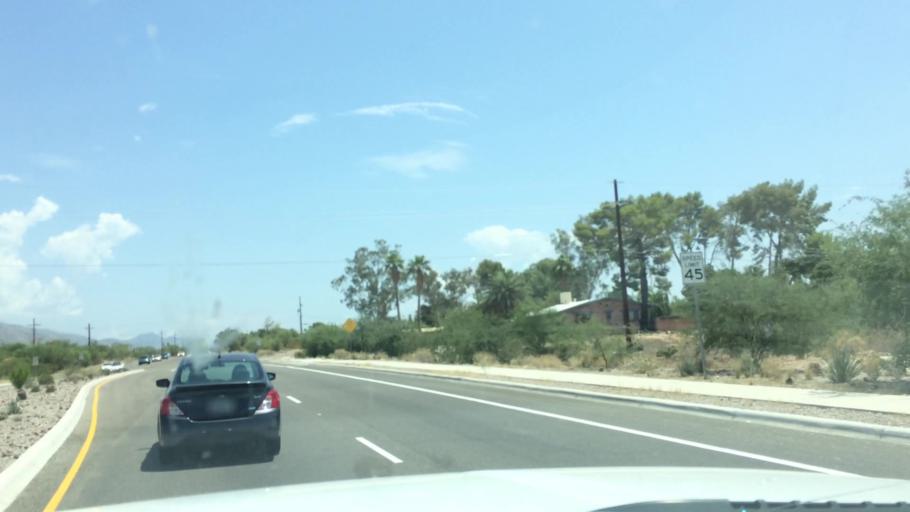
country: US
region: Arizona
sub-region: Pima County
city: Casas Adobes
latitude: 32.3231
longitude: -110.9941
